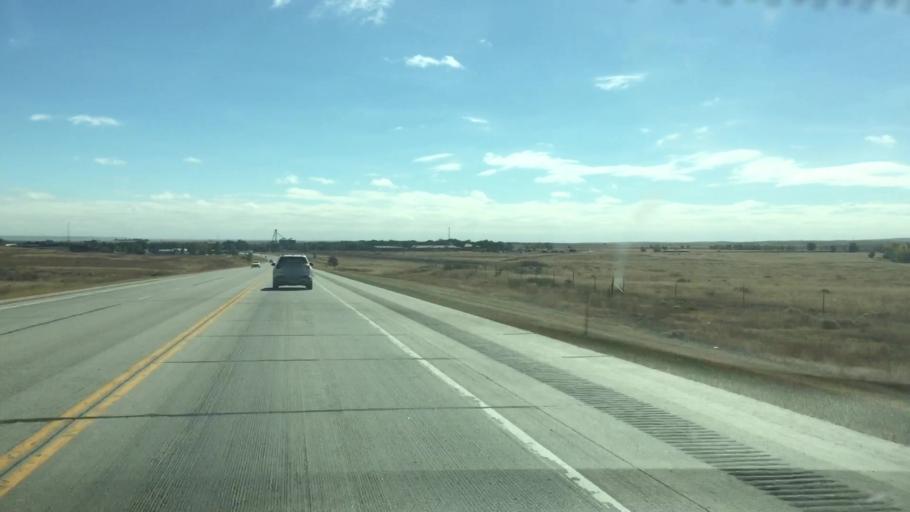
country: US
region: Colorado
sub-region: Lincoln County
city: Hugo
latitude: 39.1410
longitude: -103.4870
